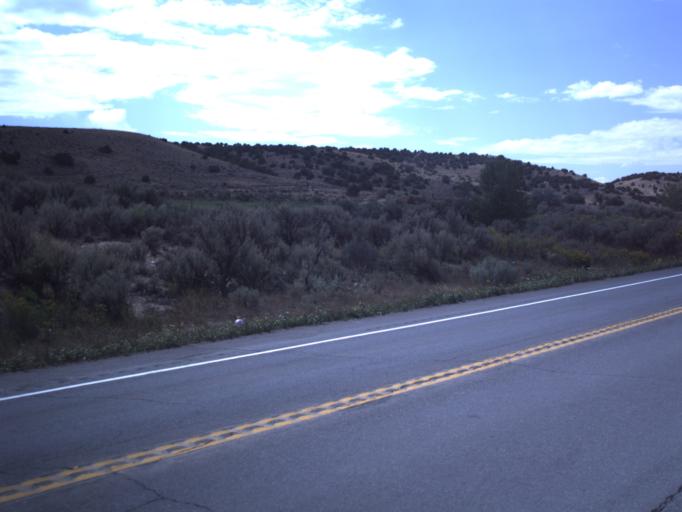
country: US
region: Utah
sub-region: Duchesne County
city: Duchesne
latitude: 40.1696
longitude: -110.3061
